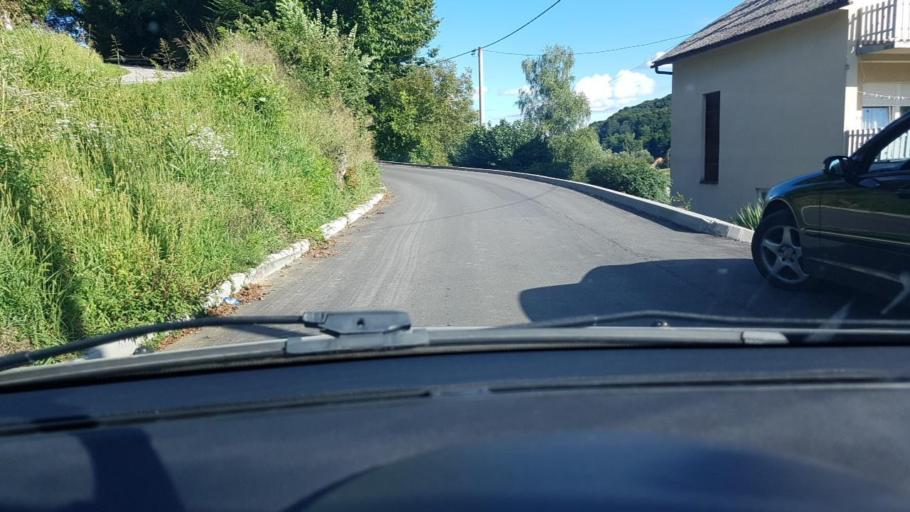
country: HR
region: Krapinsko-Zagorska
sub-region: Grad Krapina
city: Krapina
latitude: 46.1277
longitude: 15.8450
